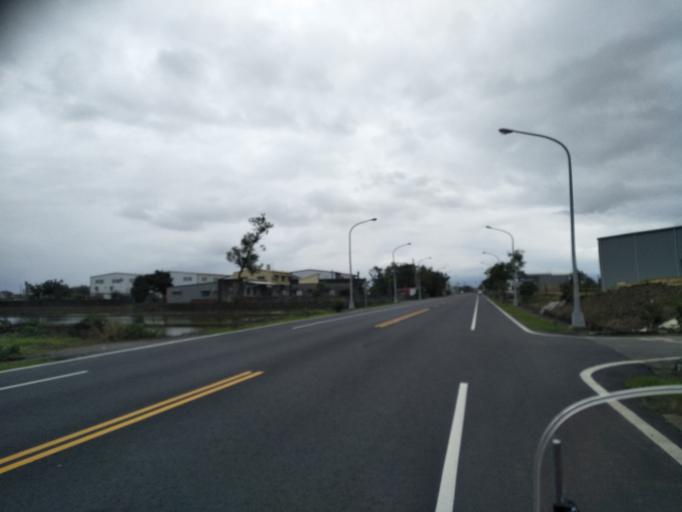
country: TW
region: Taiwan
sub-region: Yilan
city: Yilan
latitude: 24.8053
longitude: 121.7897
